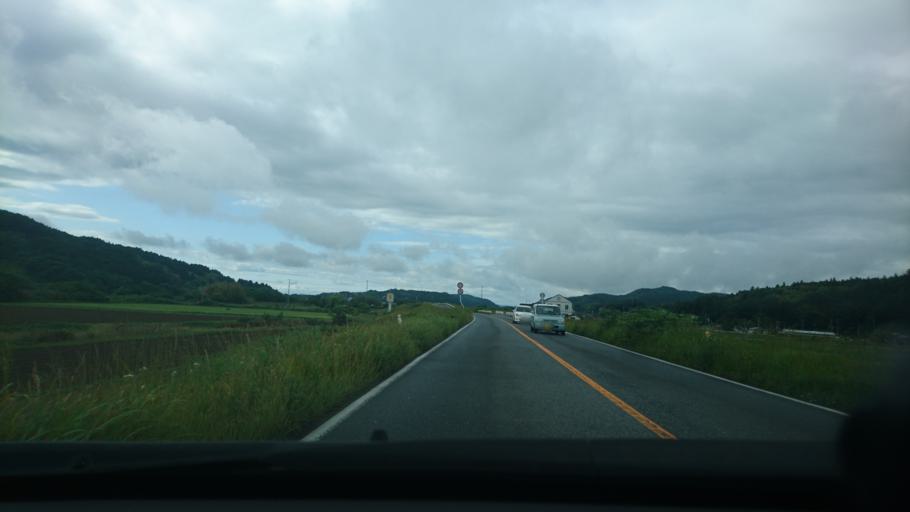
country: JP
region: Miyagi
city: Wakuya
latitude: 38.6375
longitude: 141.2887
